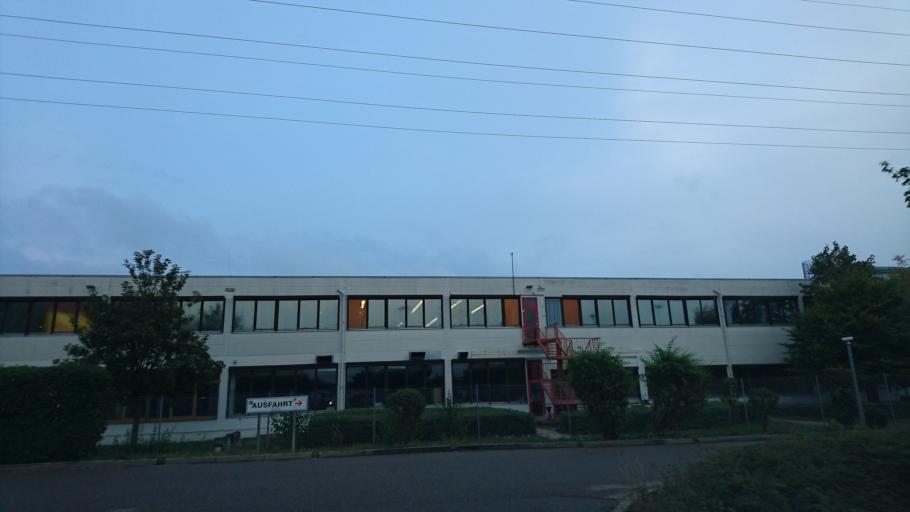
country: DE
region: Bavaria
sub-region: Swabia
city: Konigsbrunn
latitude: 48.3212
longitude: 10.8906
